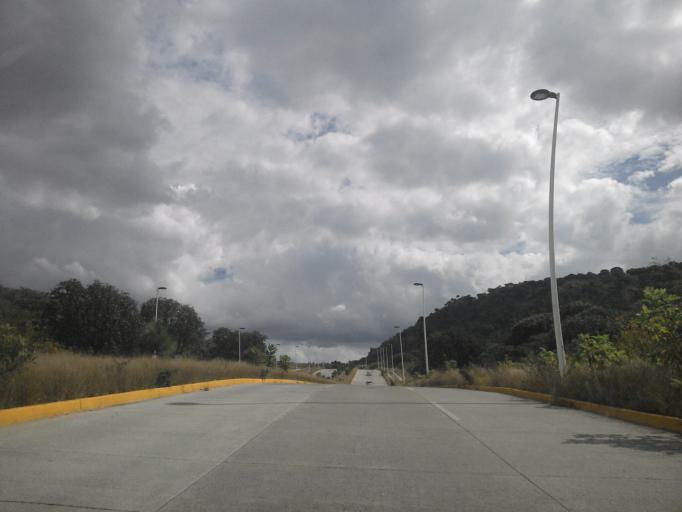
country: MX
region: Jalisco
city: Guadalajara
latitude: 20.6701
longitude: -103.4610
